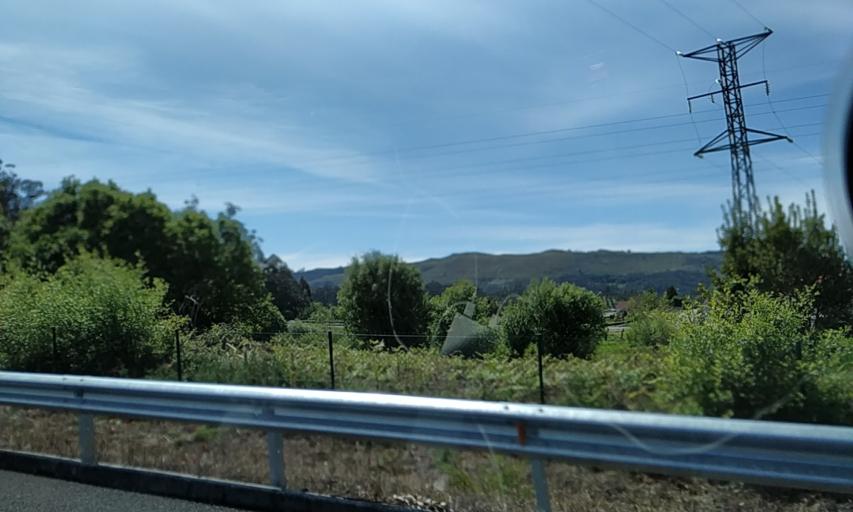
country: ES
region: Galicia
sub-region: Provincia de Pontevedra
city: Valga
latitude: 42.6654
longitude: -8.6337
